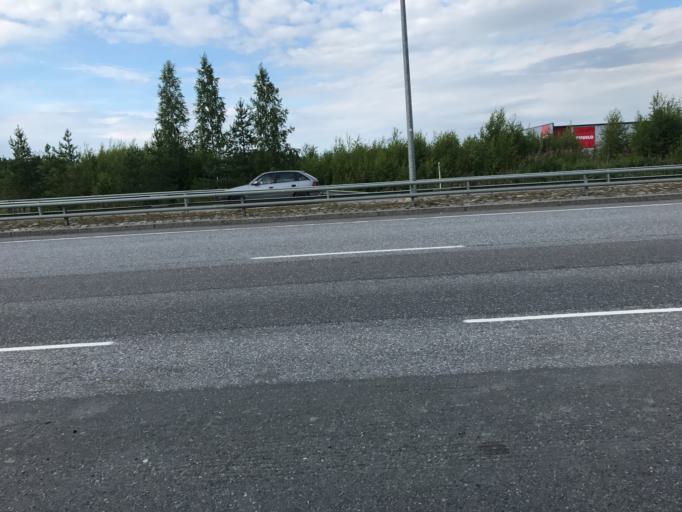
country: FI
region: Pirkanmaa
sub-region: Tampere
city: Lempaeaelae
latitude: 61.3661
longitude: 23.7956
